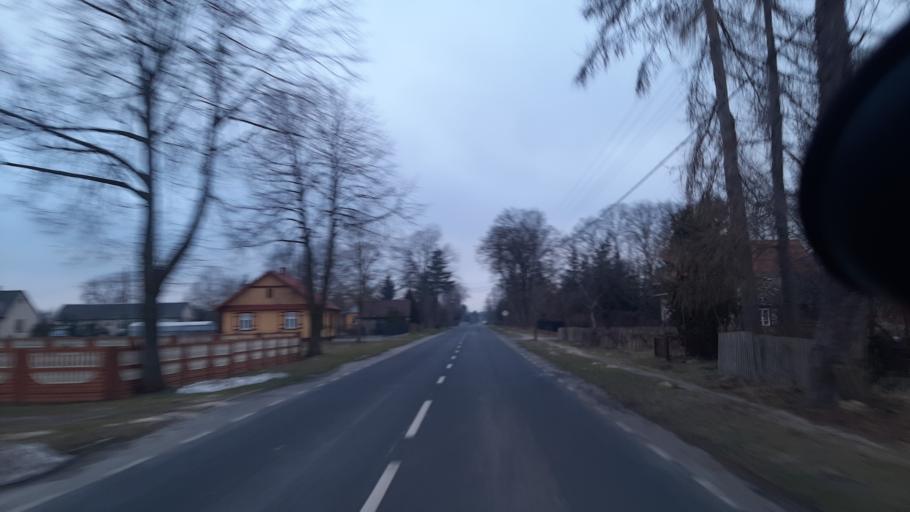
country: PL
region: Lublin Voivodeship
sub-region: Powiat parczewski
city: Debowa Kloda
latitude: 51.6372
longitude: 23.0470
